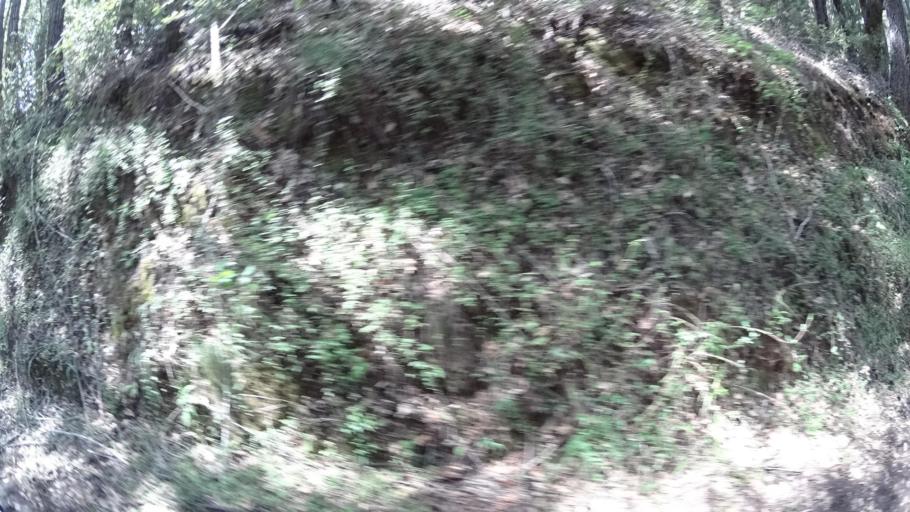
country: US
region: California
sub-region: Humboldt County
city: Redway
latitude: 40.2118
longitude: -123.6659
